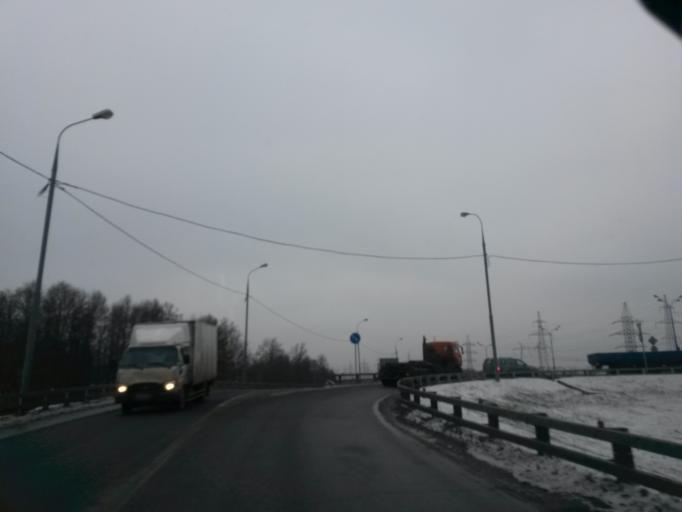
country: RU
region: Moscow
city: Mikhalkovo
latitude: 55.6692
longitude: 37.4259
